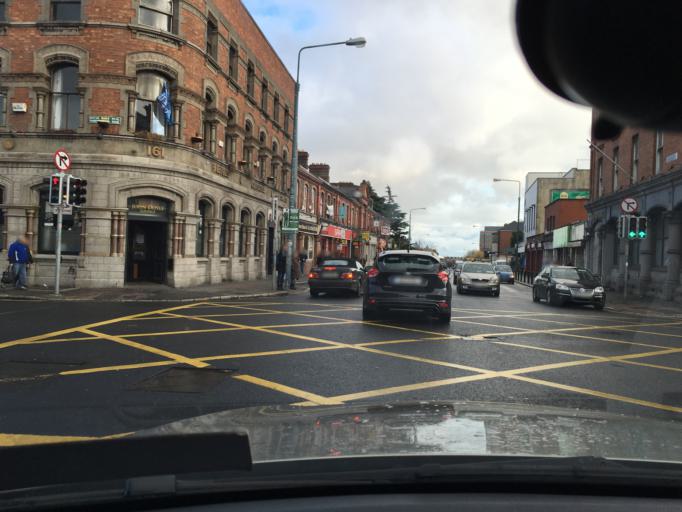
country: IE
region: Leinster
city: Glasnevin
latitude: 53.3608
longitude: -6.2728
